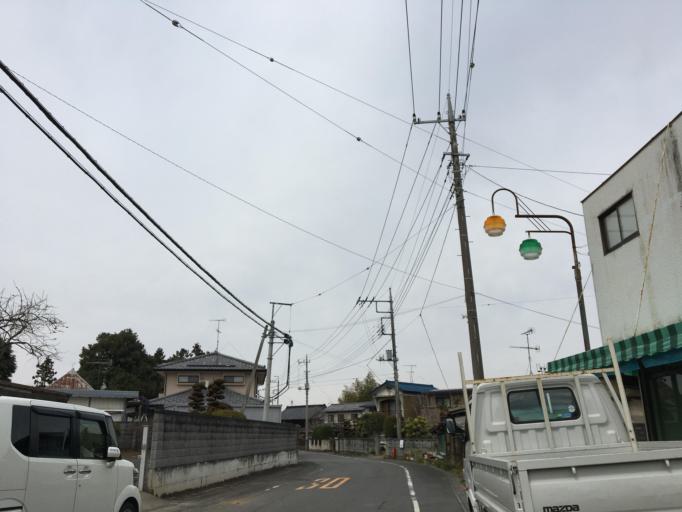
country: JP
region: Saitama
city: Kodamacho-kodamaminami
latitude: 36.1673
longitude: 139.1680
